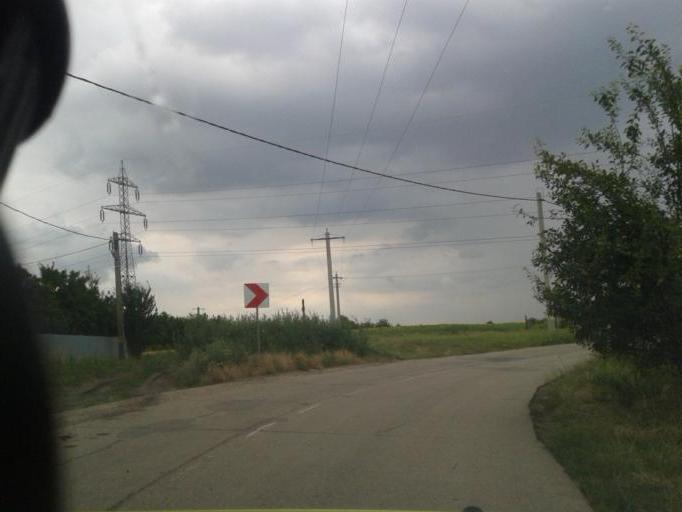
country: RO
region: Ialomita
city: Sinesti
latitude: 44.5424
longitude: 26.4263
